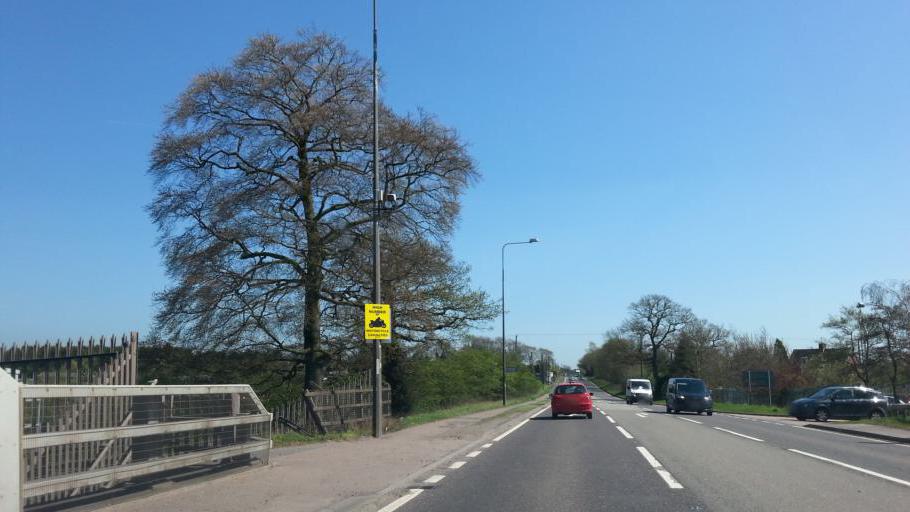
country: GB
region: England
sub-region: Staffordshire
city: Penkridge
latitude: 52.6927
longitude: -2.1282
